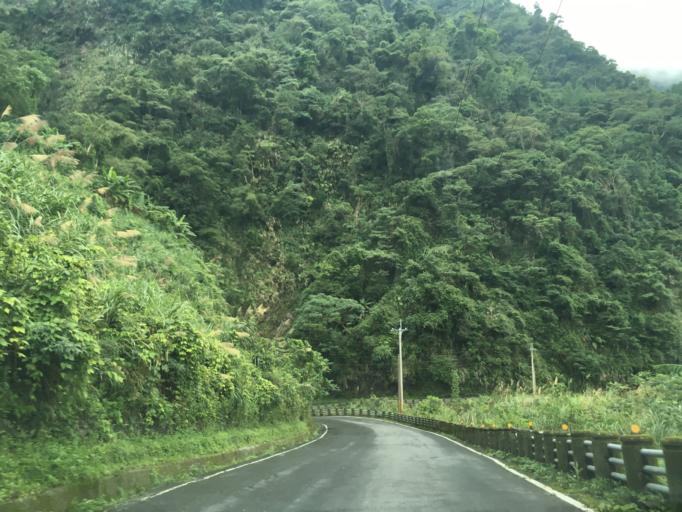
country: TW
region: Taiwan
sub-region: Chiayi
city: Jiayi Shi
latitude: 23.4431
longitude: 120.6588
